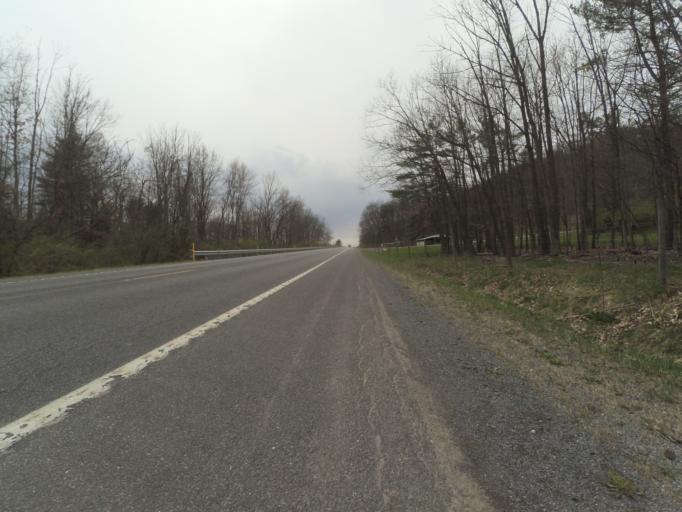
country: US
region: Pennsylvania
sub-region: Centre County
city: Milesburg
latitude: 40.9861
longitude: -77.7209
